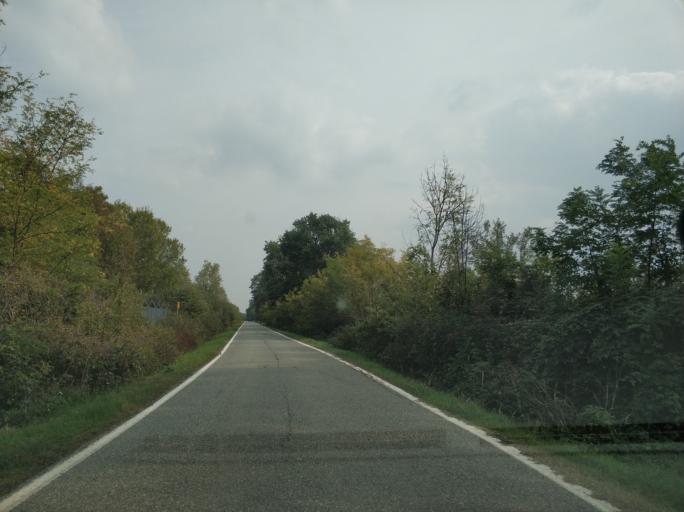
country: IT
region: Piedmont
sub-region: Provincia di Torino
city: San Francesco al Campo
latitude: 45.2421
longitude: 7.6785
